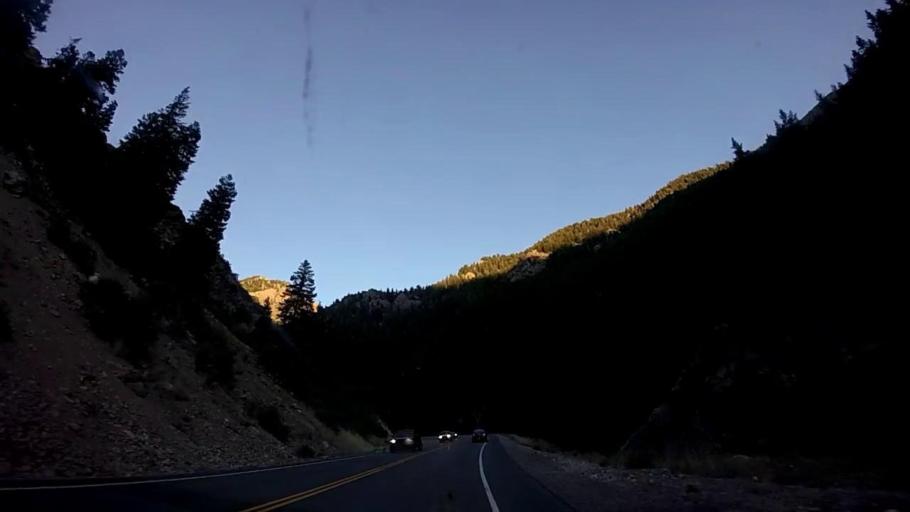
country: US
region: Utah
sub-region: Salt Lake County
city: Mount Olympus
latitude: 40.6337
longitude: -111.7074
